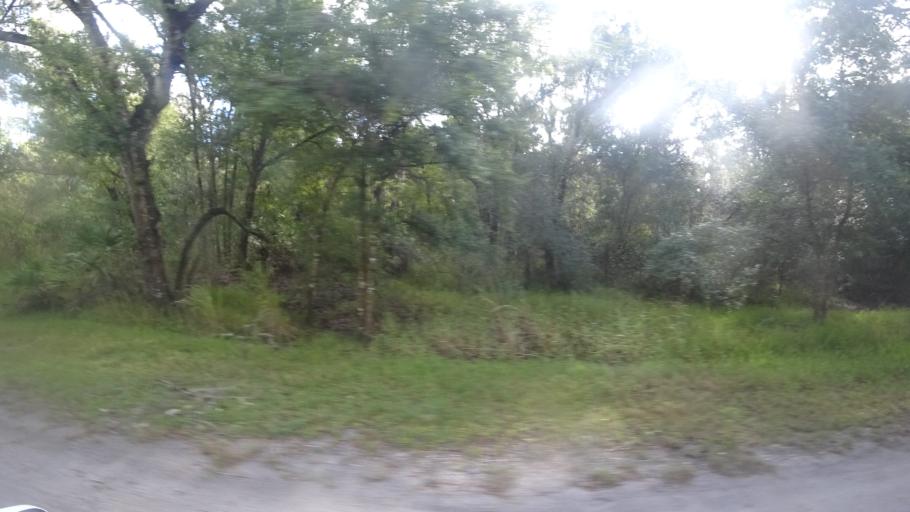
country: US
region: Florida
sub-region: Hillsborough County
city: Sun City Center
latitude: 27.5949
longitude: -82.3637
